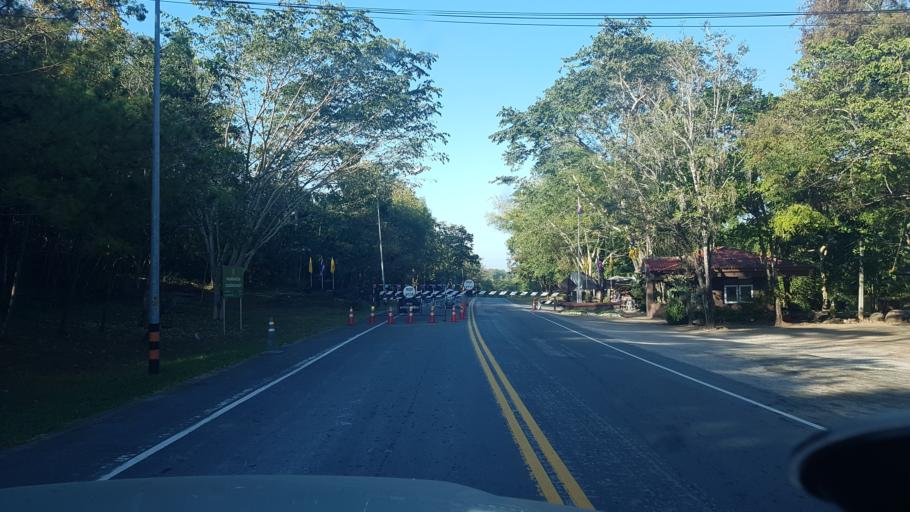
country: TH
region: Phetchabun
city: Lom Sak
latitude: 16.7372
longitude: 101.4400
